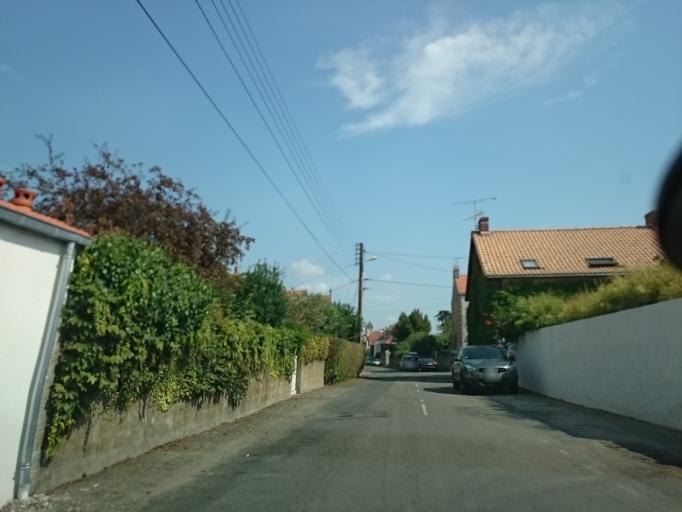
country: FR
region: Pays de la Loire
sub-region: Departement de la Loire-Atlantique
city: La Montagne
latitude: 47.1924
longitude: -1.6893
